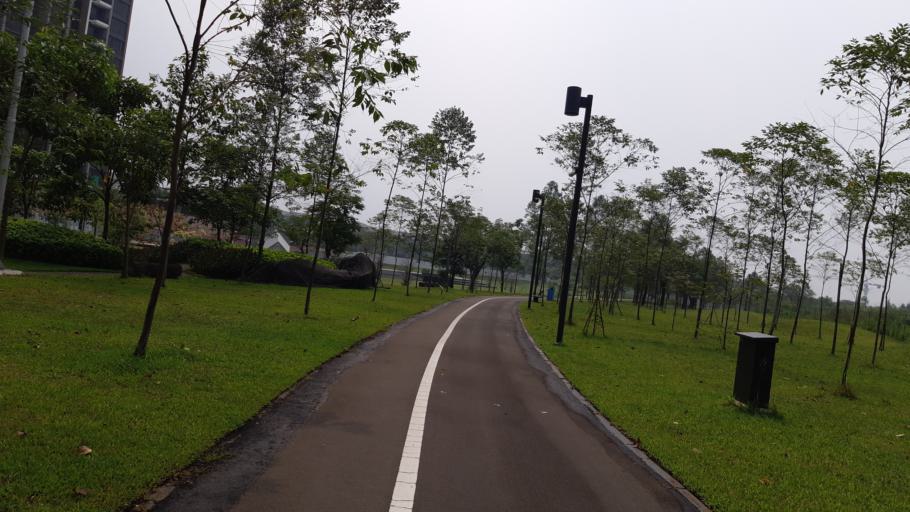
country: ID
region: West Java
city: Serpong
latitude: -6.2966
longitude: 106.6514
